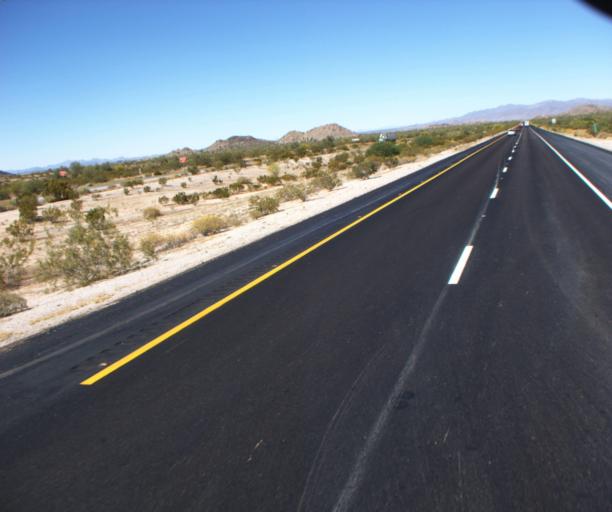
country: US
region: Arizona
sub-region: Maricopa County
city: Buckeye
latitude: 33.2760
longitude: -112.6317
